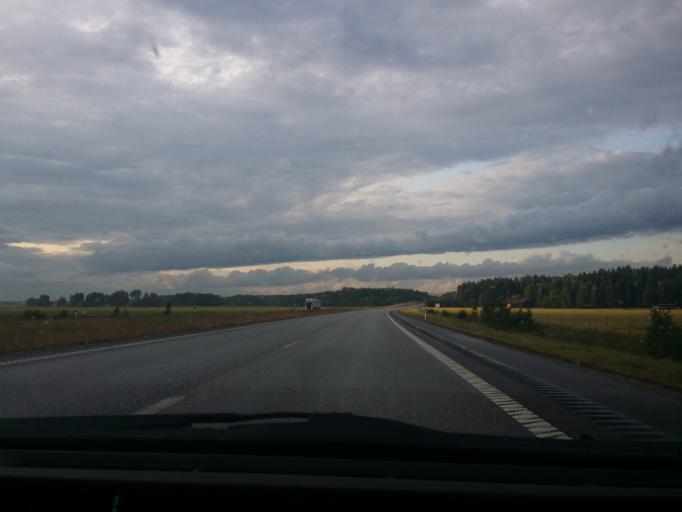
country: SE
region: Vaestmanland
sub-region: Arboga Kommun
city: Arboga
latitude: 59.4539
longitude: 15.8979
